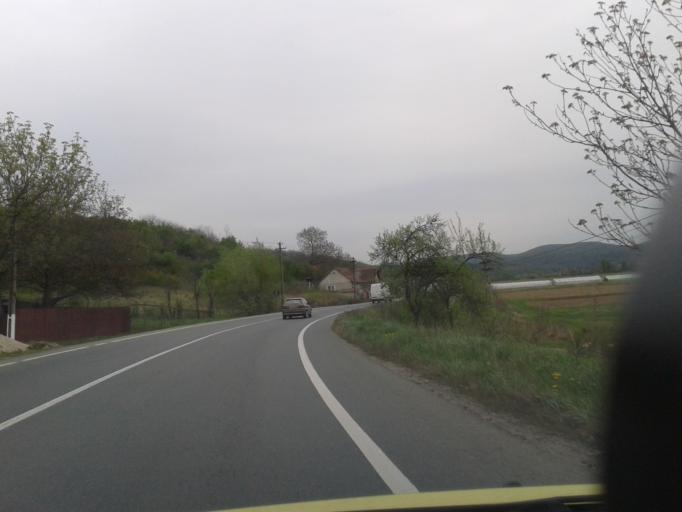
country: RO
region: Arad
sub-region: Comuna Barzava
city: Barzava
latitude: 46.1043
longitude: 22.0013
